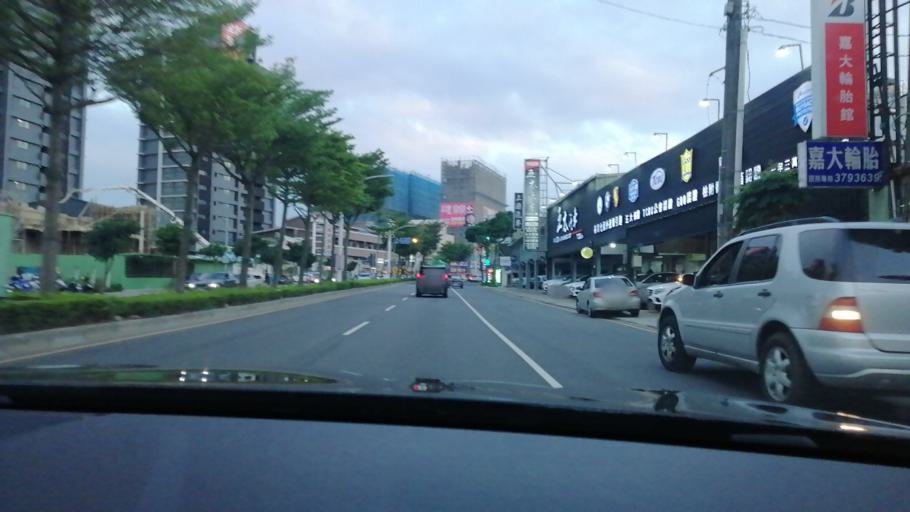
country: TW
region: Taiwan
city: Taoyuan City
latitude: 24.9999
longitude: 121.2876
